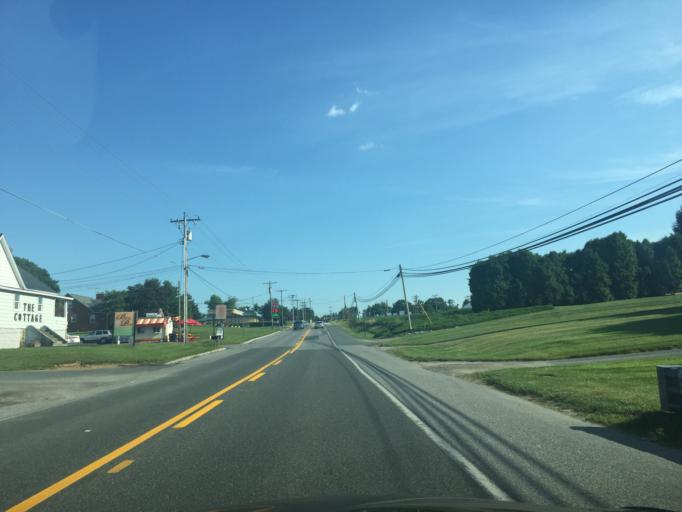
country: US
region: Maryland
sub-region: Harford County
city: Jarrettsville
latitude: 39.6076
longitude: -76.4780
